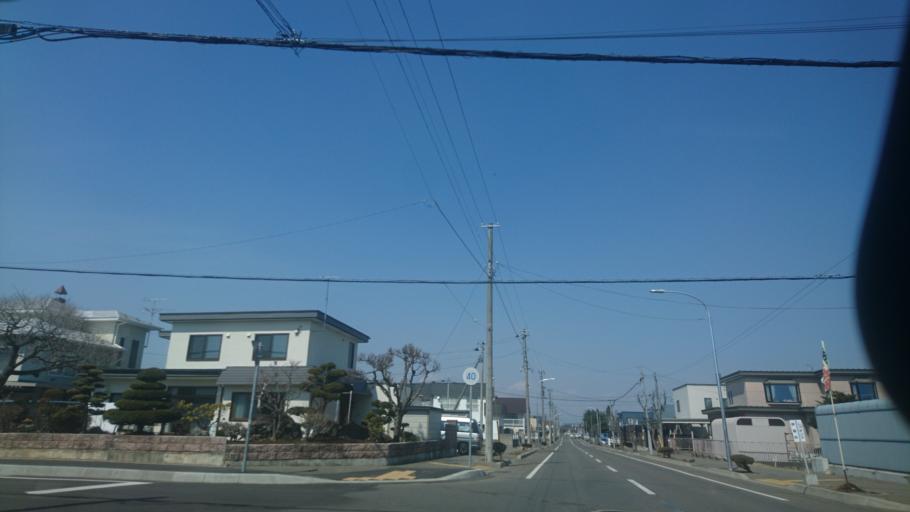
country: JP
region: Hokkaido
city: Obihiro
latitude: 42.9136
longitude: 143.0588
